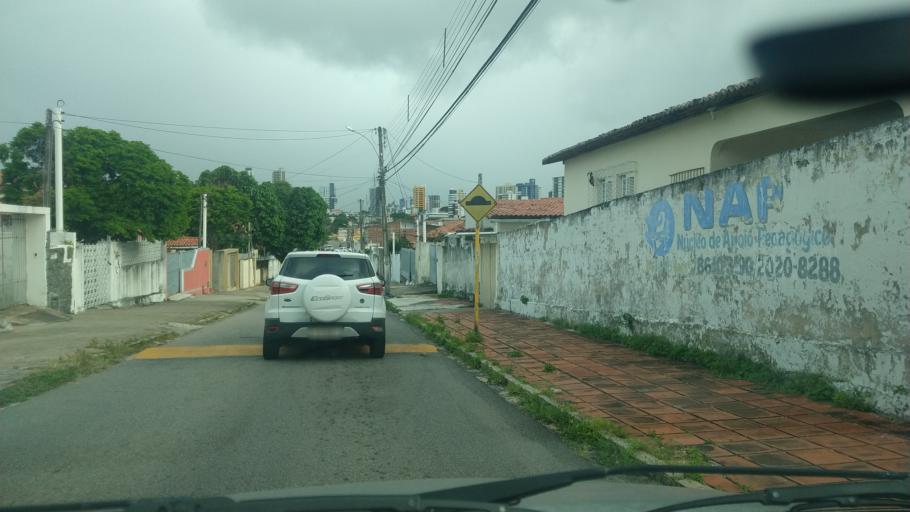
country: BR
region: Rio Grande do Norte
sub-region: Natal
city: Natal
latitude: -5.8286
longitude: -35.2088
